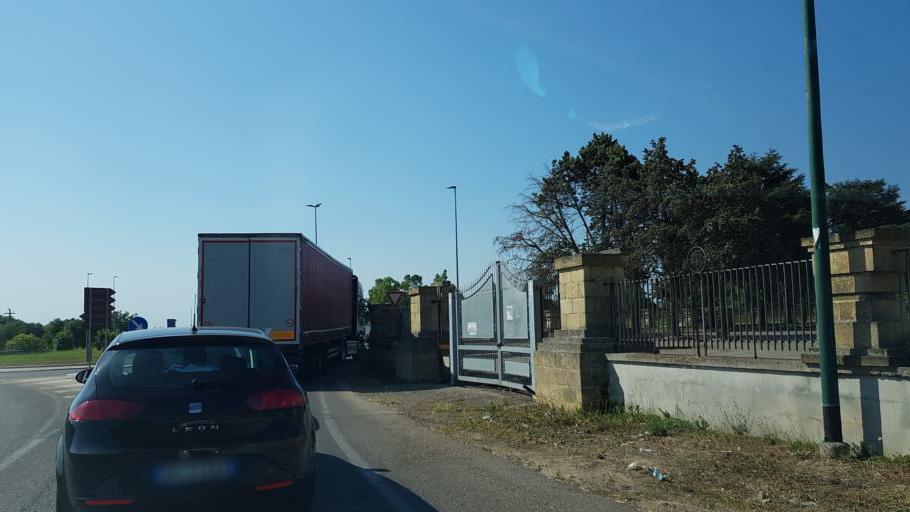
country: IT
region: Apulia
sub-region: Provincia di Lecce
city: Guagnano
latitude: 40.4128
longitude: 17.9591
